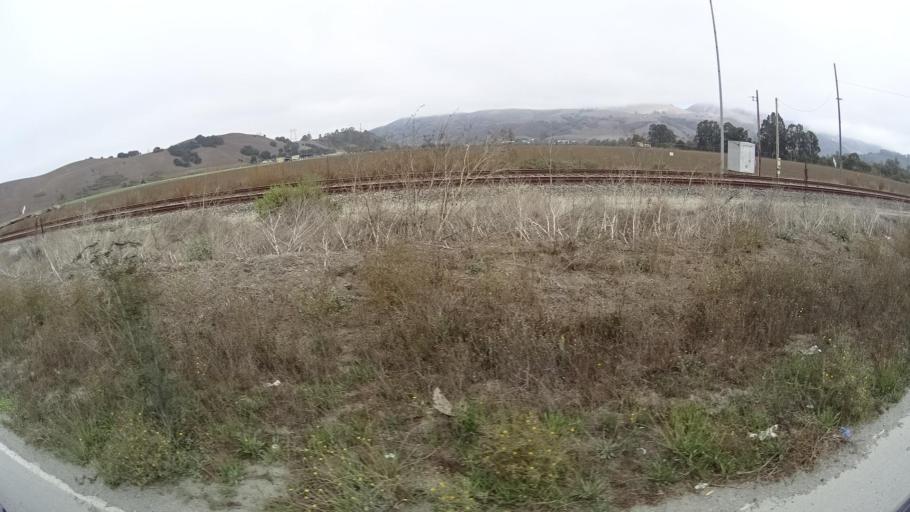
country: US
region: California
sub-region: San Benito County
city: Aromas
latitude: 36.8910
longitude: -121.6482
